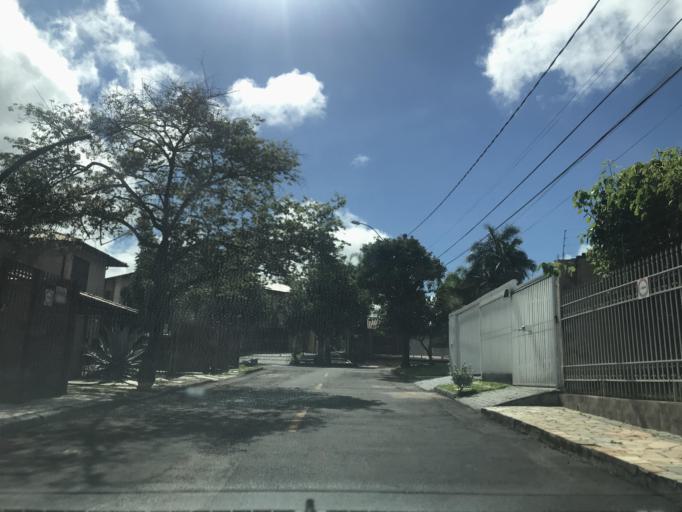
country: BR
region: Federal District
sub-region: Brasilia
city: Brasilia
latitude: -15.7236
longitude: -47.8768
